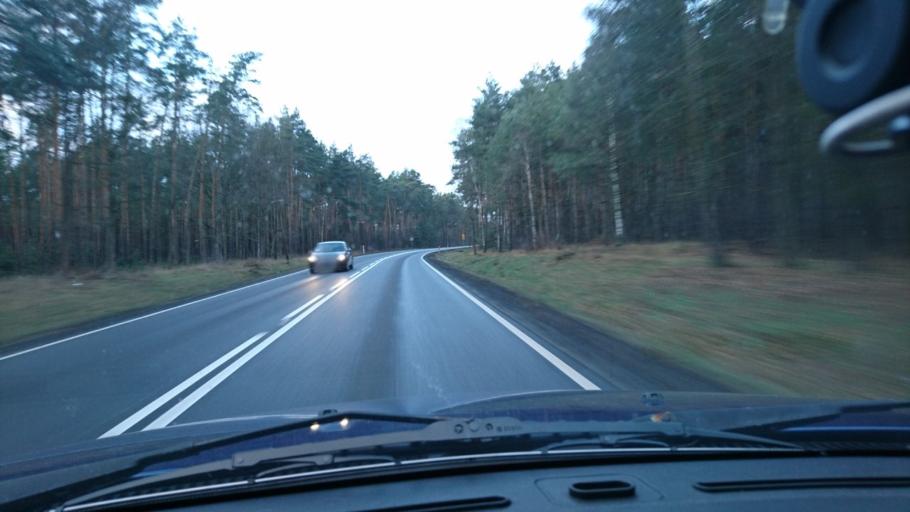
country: PL
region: Greater Poland Voivodeship
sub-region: Powiat kepinski
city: Kepno
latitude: 51.3369
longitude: 17.9542
